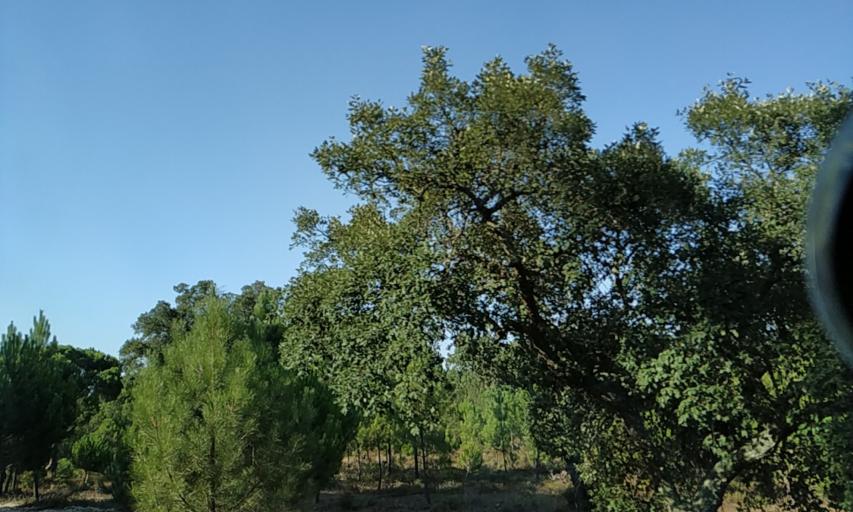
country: PT
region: Santarem
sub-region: Coruche
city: Coruche
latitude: 38.9772
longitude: -8.5418
